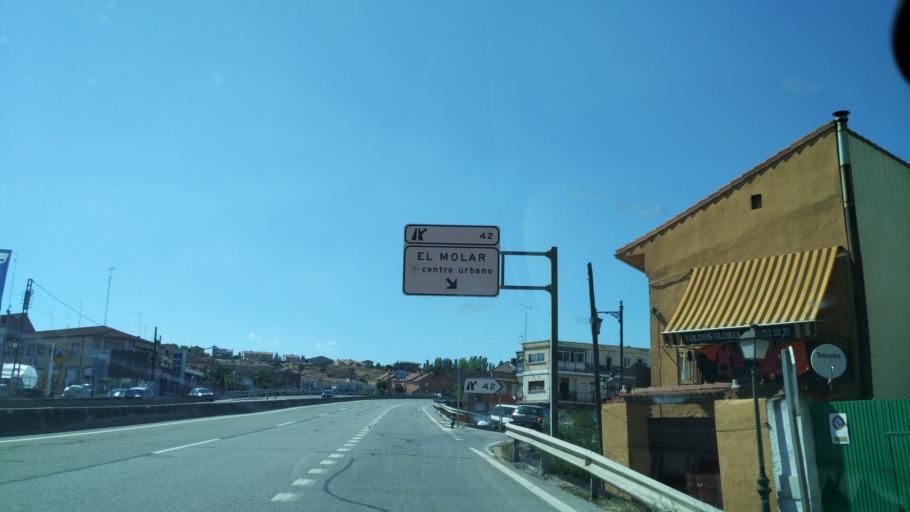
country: ES
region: Madrid
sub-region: Provincia de Madrid
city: El Molar
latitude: 40.7306
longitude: -3.5823
